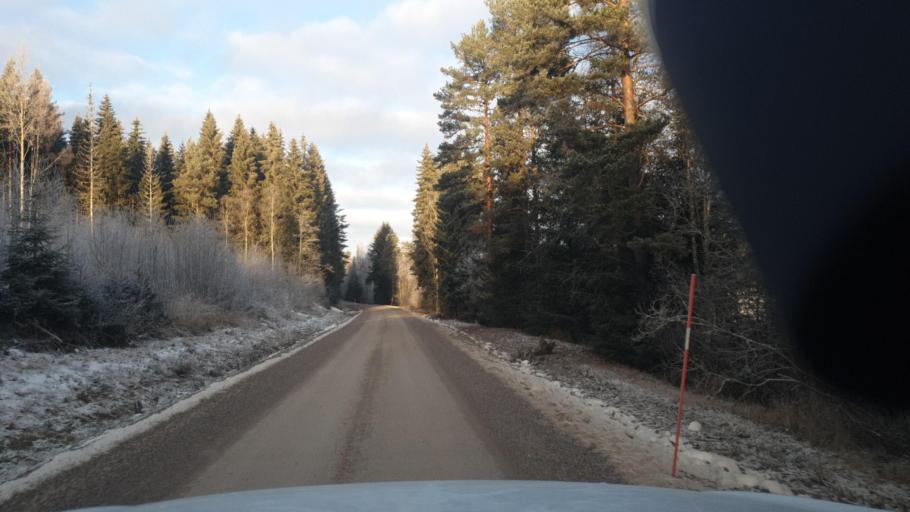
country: SE
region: Vaermland
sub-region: Eda Kommun
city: Charlottenberg
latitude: 60.0814
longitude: 12.5227
